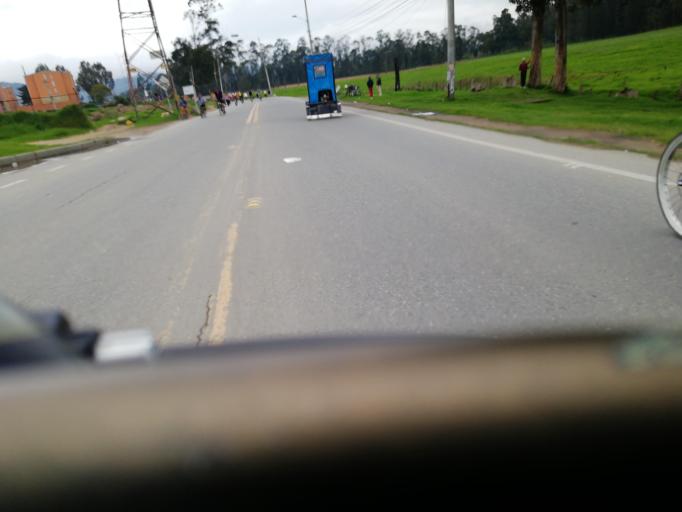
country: CO
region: Cundinamarca
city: Soacha
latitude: 4.5817
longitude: -74.2370
